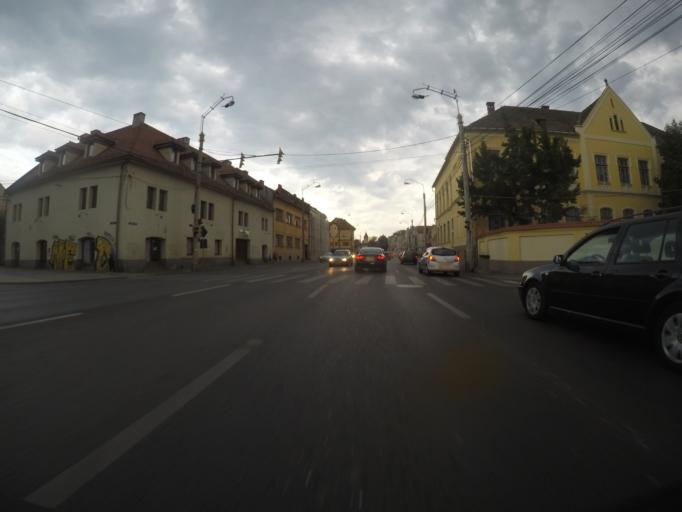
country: RO
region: Sibiu
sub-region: Municipiul Sibiu
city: Sibiu
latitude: 45.8001
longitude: 24.1571
